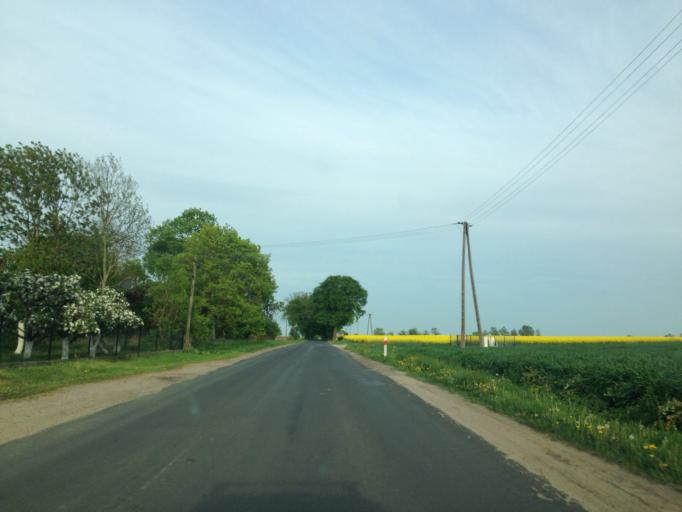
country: PL
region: Kujawsko-Pomorskie
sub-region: Powiat brodnicki
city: Bobrowo
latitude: 53.2279
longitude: 19.1930
